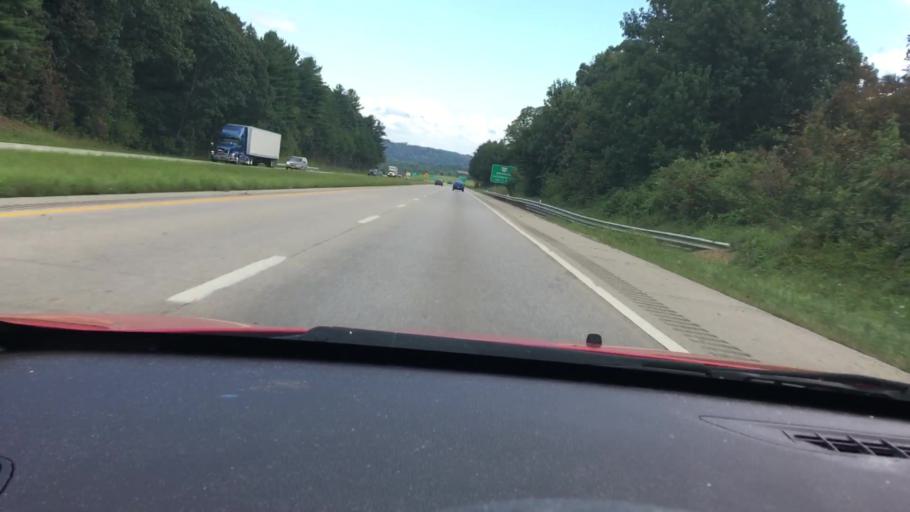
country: US
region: Ohio
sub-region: Athens County
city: The Plains
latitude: 39.3725
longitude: -82.1259
